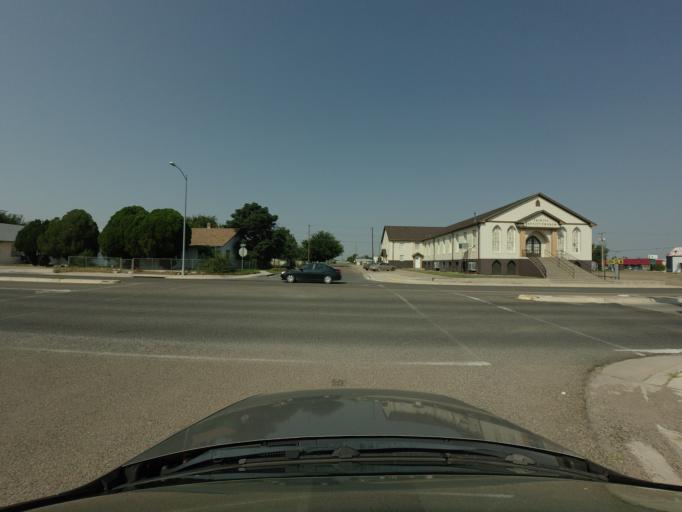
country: US
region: New Mexico
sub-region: Quay County
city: Tucumcari
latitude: 35.1709
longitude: -103.7247
